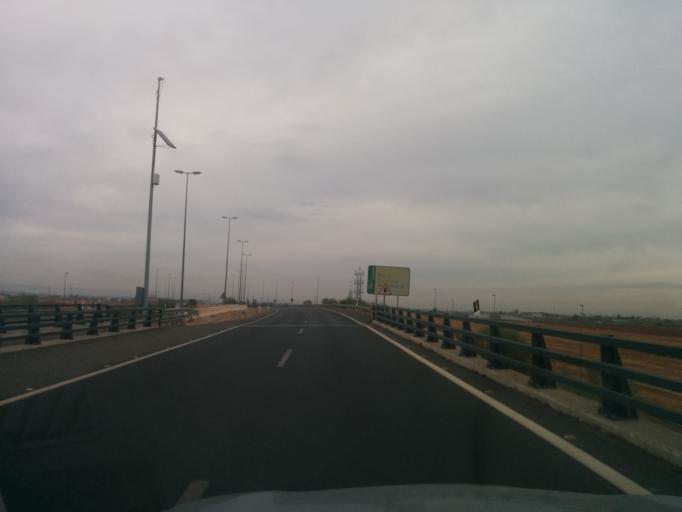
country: ES
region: Andalusia
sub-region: Provincia de Sevilla
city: La Algaba
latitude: 37.4364
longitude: -5.9728
